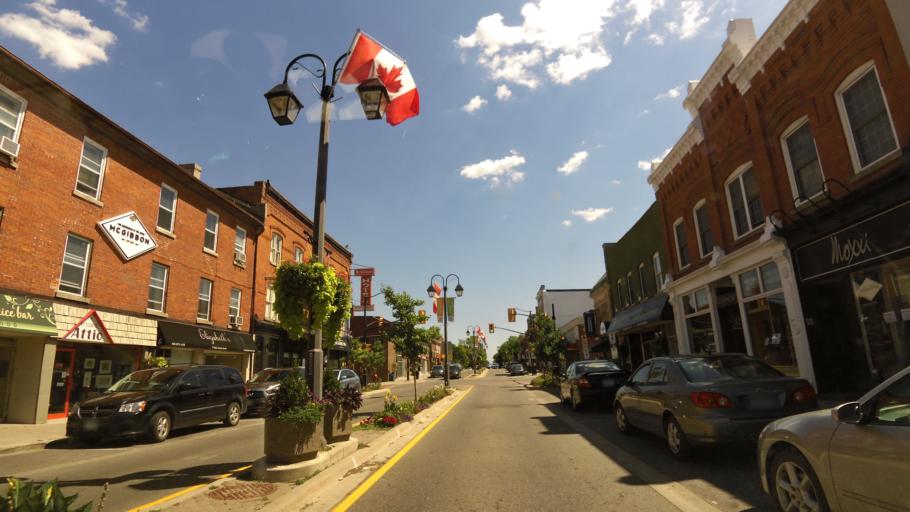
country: CA
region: Ontario
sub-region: Halton
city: Milton
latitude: 43.6497
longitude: -79.9266
